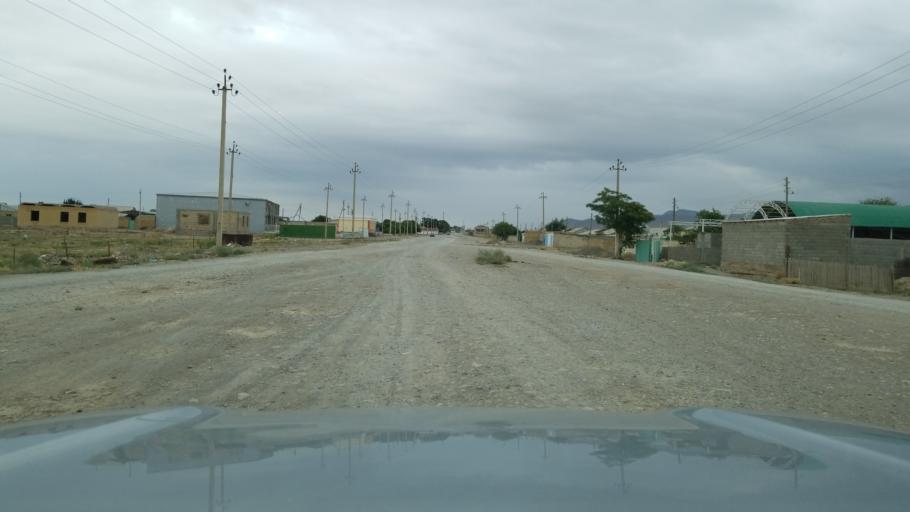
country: TM
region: Balkan
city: Serdar
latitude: 38.9870
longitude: 56.2519
